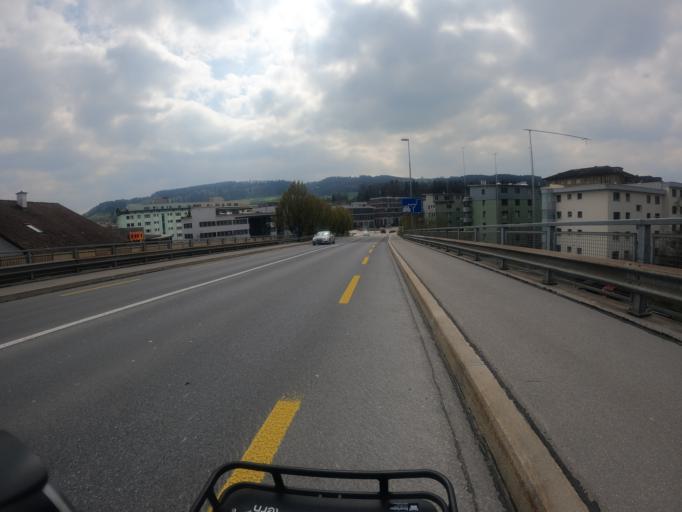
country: CH
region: Lucerne
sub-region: Lucerne-Land District
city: Meierskappel
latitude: 47.1410
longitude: 8.4261
